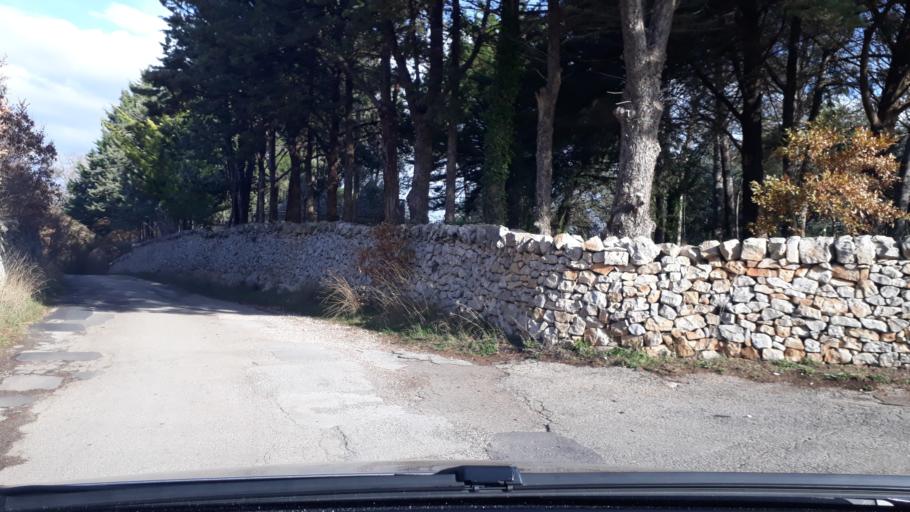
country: IT
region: Apulia
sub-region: Provincia di Brindisi
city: Cisternino
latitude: 40.6933
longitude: 17.4150
